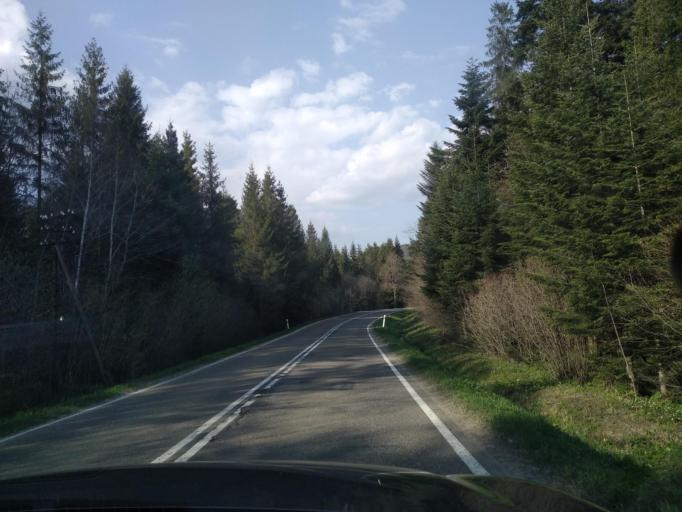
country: PL
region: Subcarpathian Voivodeship
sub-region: Powiat leski
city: Baligrod
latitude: 49.2985
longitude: 22.2721
